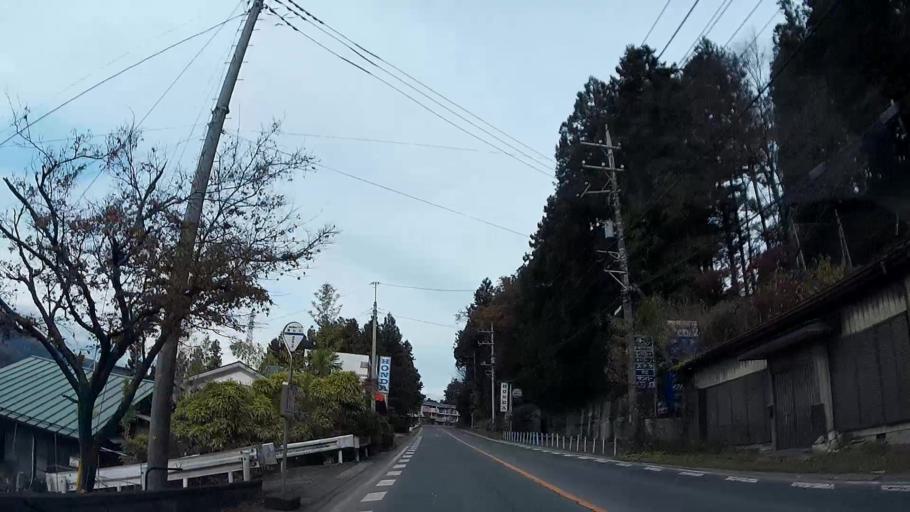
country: JP
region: Saitama
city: Chichibu
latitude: 35.9657
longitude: 139.0597
